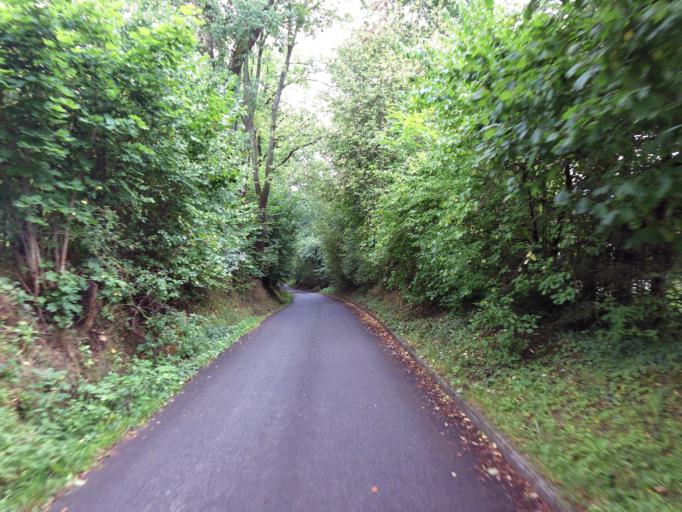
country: CZ
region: Jihocesky
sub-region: Okres Ceske Budejovice
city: Nove Hrady
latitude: 48.7848
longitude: 14.7852
